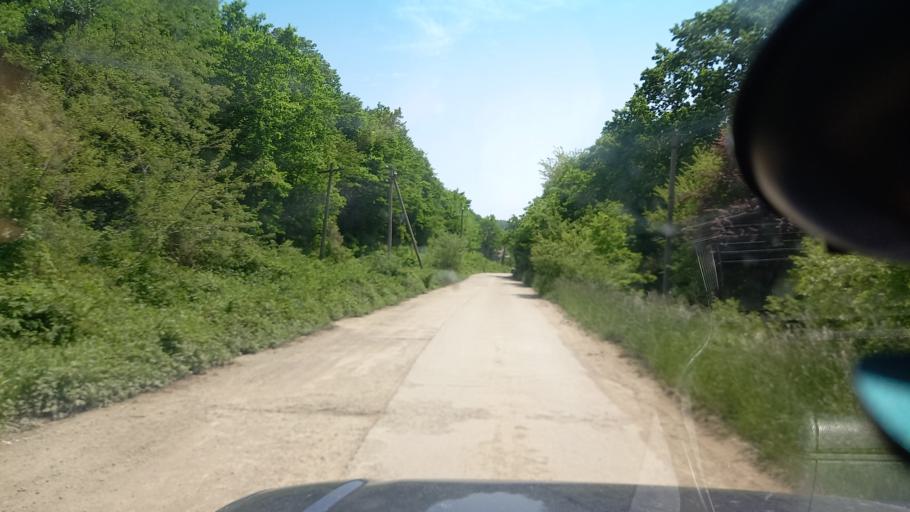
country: RU
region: Krasnodarskiy
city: Tuapse
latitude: 44.2470
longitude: 39.2391
